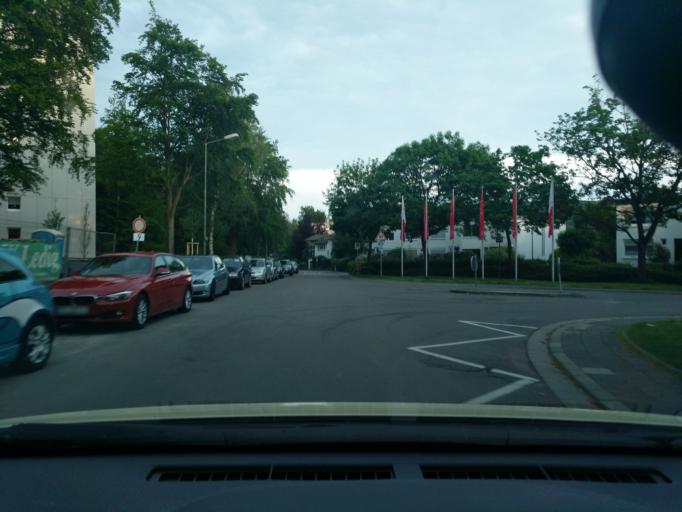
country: DE
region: Rheinland-Pfalz
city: Kaiserslautern
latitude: 49.4321
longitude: 7.7764
